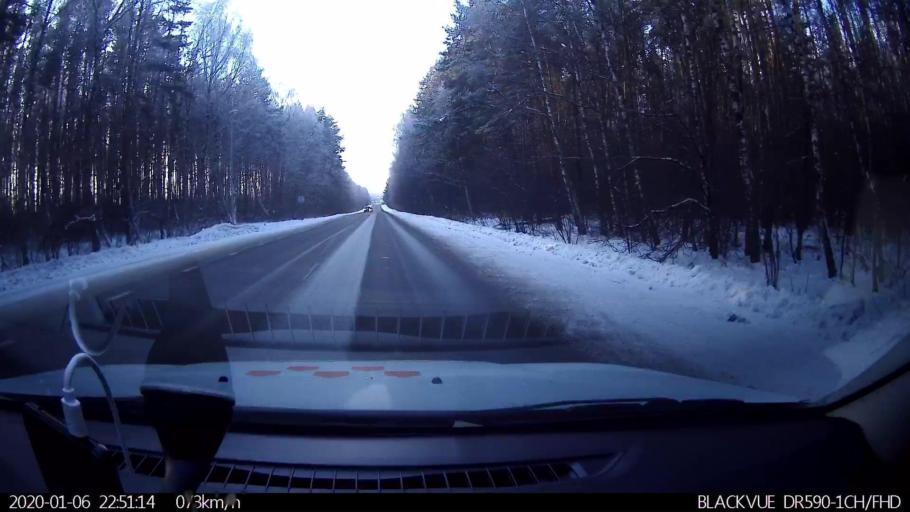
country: RU
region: Nizjnij Novgorod
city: Bogorodsk
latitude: 56.1314
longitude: 43.6039
